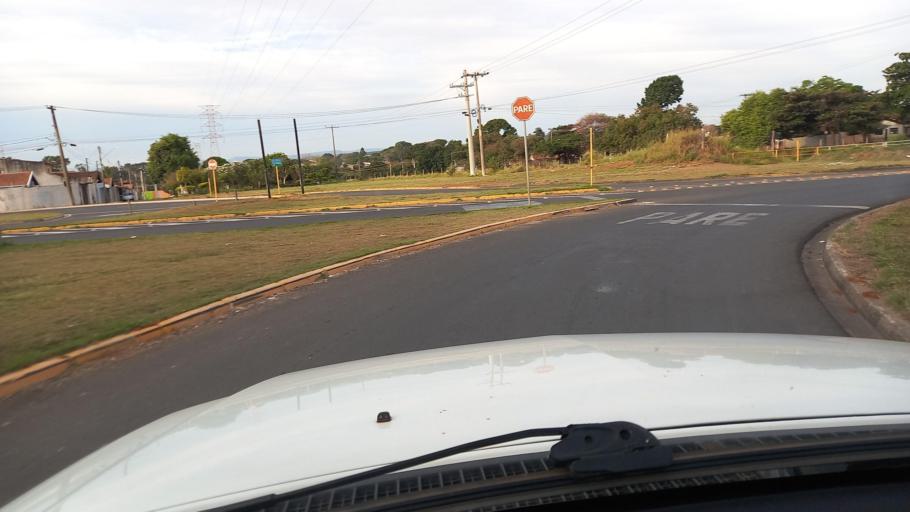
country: BR
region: Sao Paulo
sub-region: Moji-Guacu
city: Mogi-Gaucu
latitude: -22.3396
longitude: -46.9432
